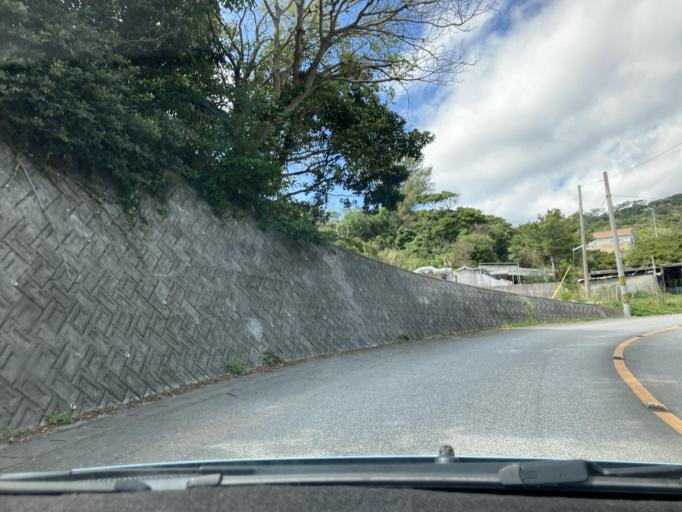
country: JP
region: Okinawa
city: Ginowan
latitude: 26.1816
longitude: 127.7662
